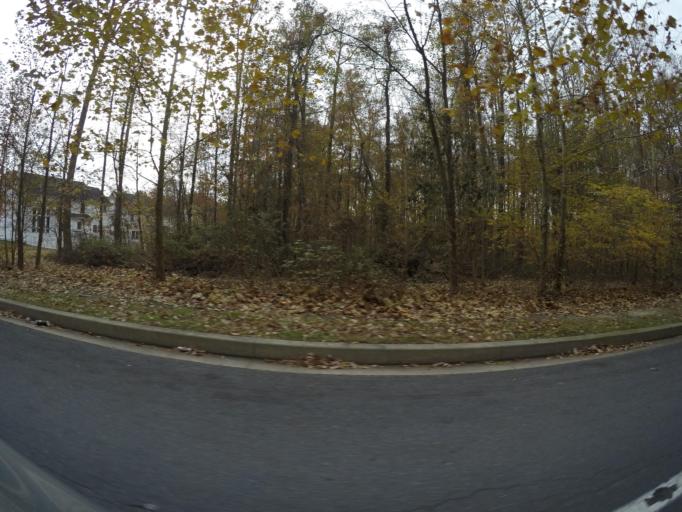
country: US
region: Maryland
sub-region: Harford County
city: Riverside
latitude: 39.4582
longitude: -76.2698
